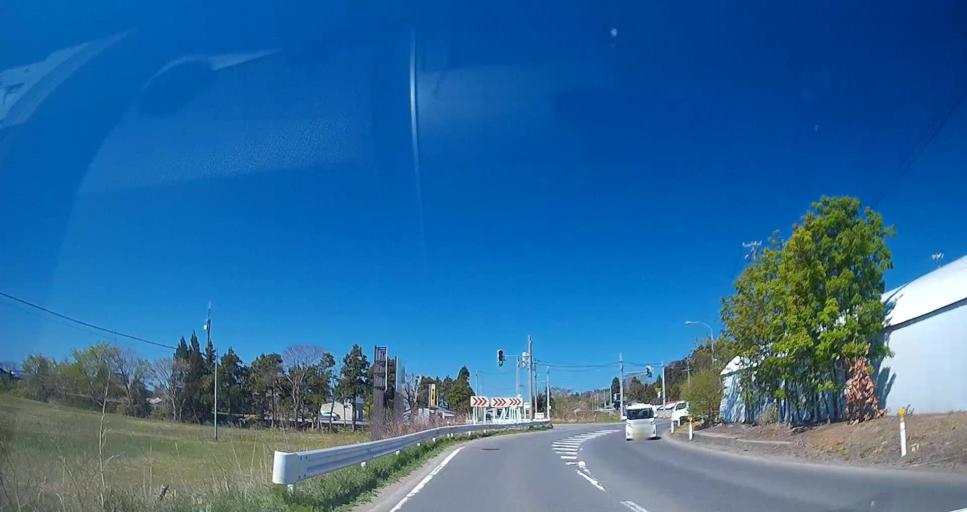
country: JP
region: Aomori
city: Misawa
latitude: 40.8454
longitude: 141.3698
